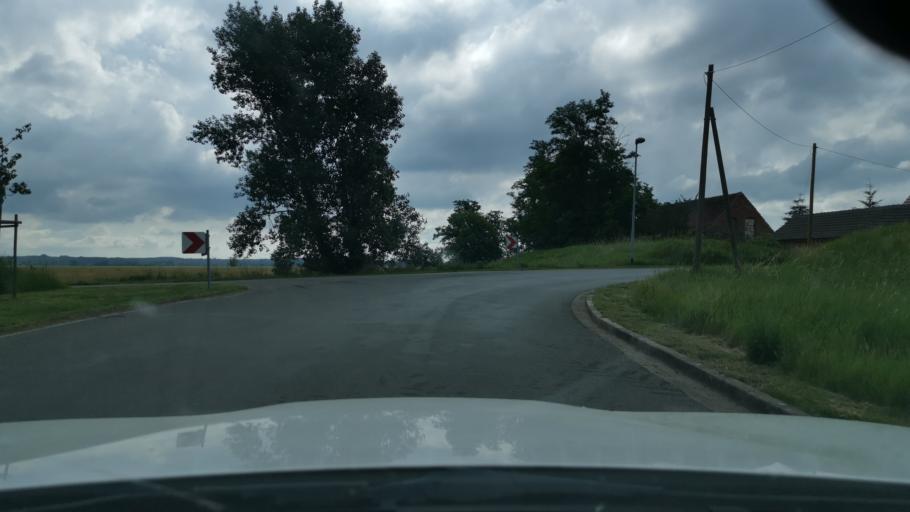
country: DE
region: Saxony
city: Torgau
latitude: 51.6153
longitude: 13.0158
